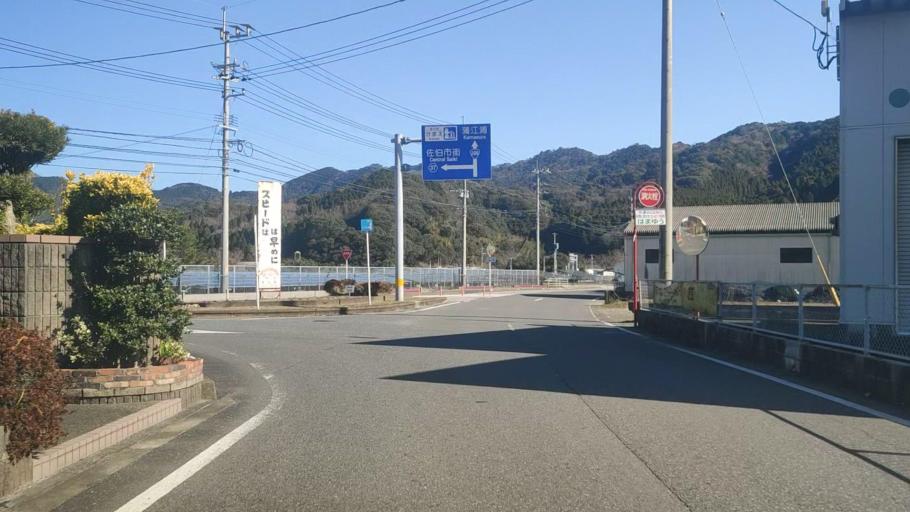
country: JP
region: Oita
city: Saiki
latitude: 32.8061
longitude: 131.8916
